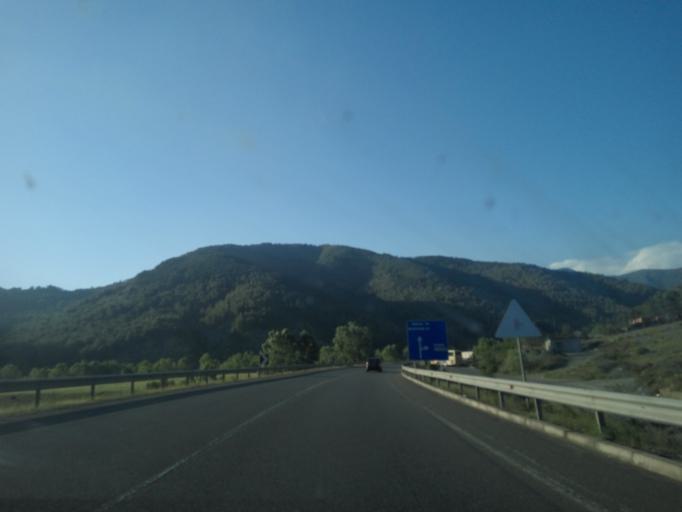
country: AL
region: Lezhe
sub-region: Rrethi i Mirdites
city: Rubik
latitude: 41.7805
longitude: 19.7838
